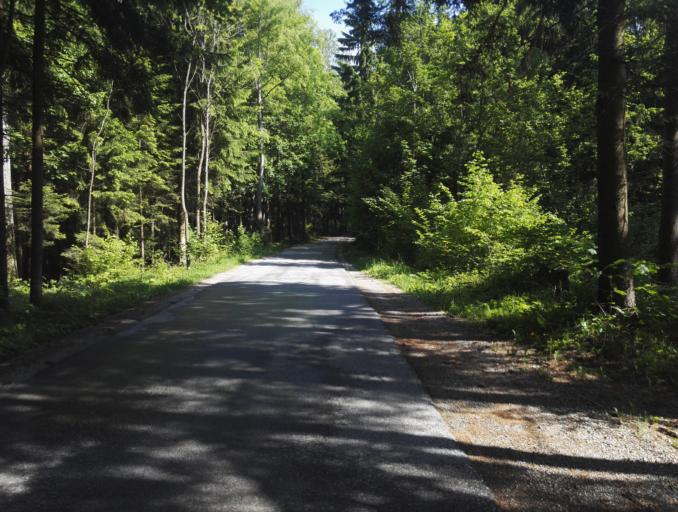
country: AT
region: Styria
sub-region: Politischer Bezirk Graz-Umgebung
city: Stattegg
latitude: 47.1719
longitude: 15.4243
